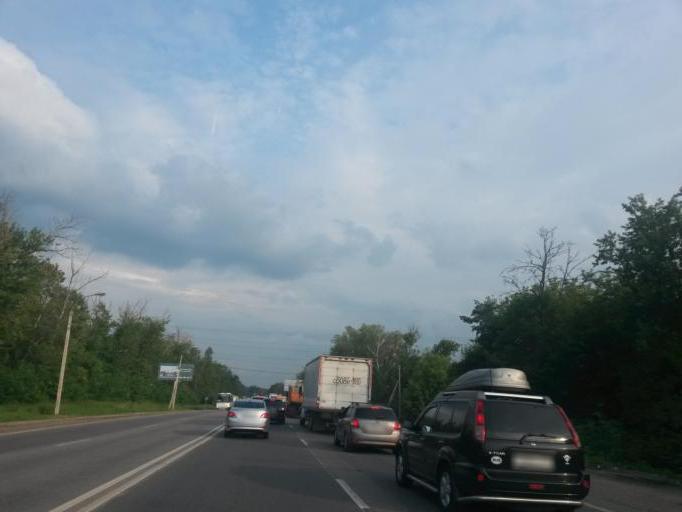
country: RU
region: Moskovskaya
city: Petrovskaya
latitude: 55.5647
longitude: 37.7675
